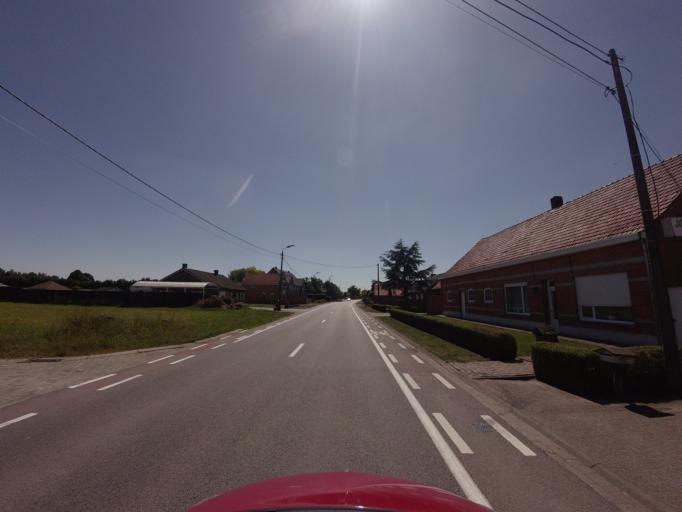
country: BE
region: Flanders
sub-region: Provincie Antwerpen
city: Ravels
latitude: 51.3840
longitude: 5.0122
